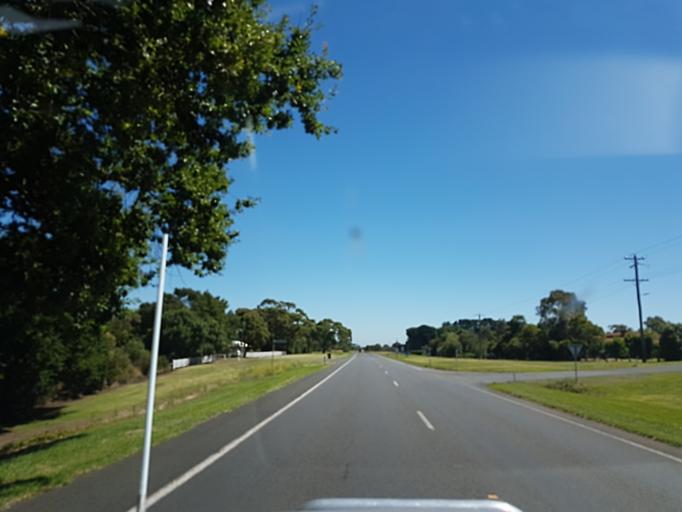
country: AU
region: Victoria
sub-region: Warrnambool
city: Allansford
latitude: -38.2468
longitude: 142.9024
